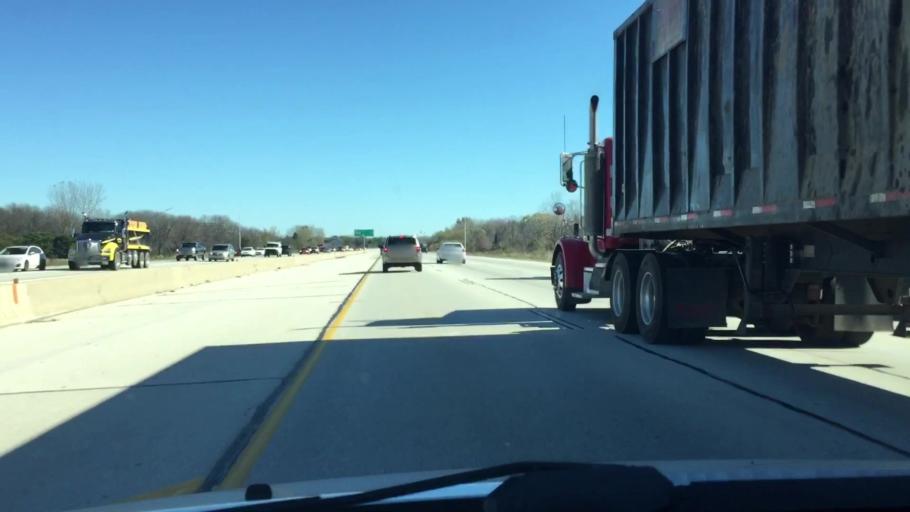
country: US
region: Wisconsin
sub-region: Waukesha County
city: Brookfield
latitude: 43.0289
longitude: -88.1413
